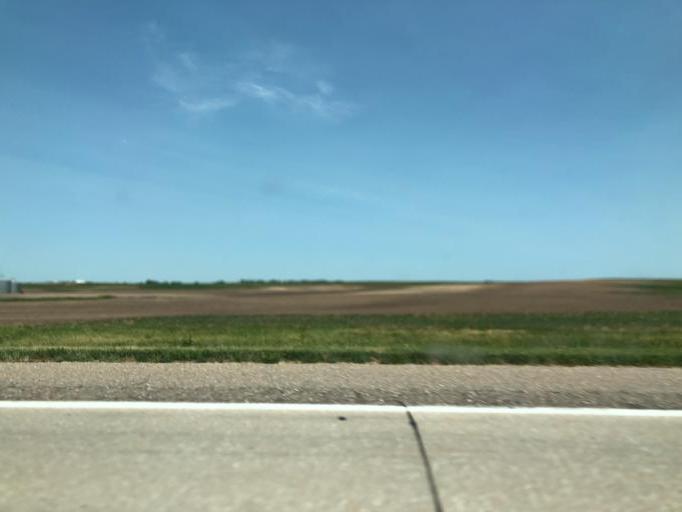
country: US
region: Nebraska
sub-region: Thayer County
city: Hebron
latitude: 40.1437
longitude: -97.5712
